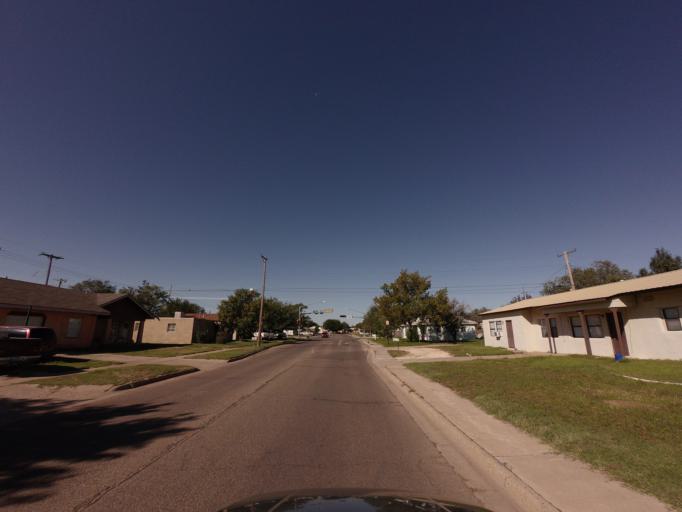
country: US
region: New Mexico
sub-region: Curry County
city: Clovis
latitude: 34.4270
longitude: -103.2133
